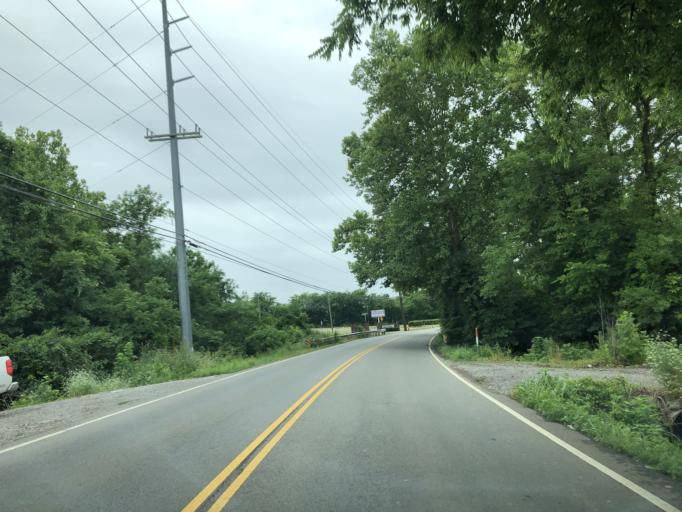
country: US
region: Tennessee
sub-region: Davidson County
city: Nashville
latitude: 36.2507
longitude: -86.7767
